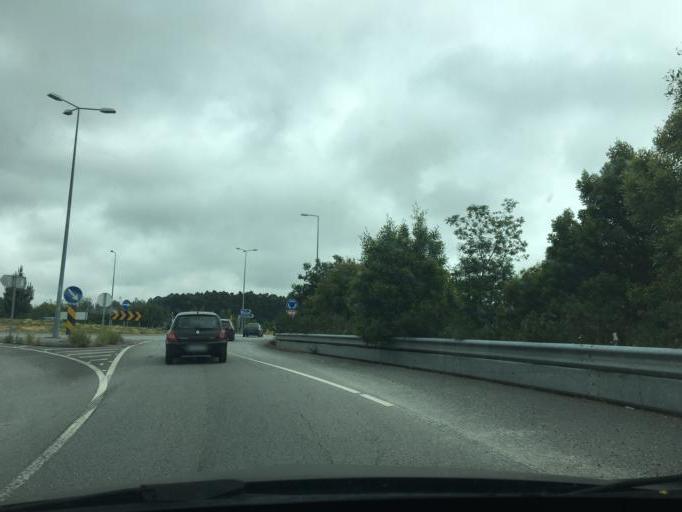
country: PT
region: Porto
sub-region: Matosinhos
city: Santa Cruz do Bispo
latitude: 41.2227
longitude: -8.6664
